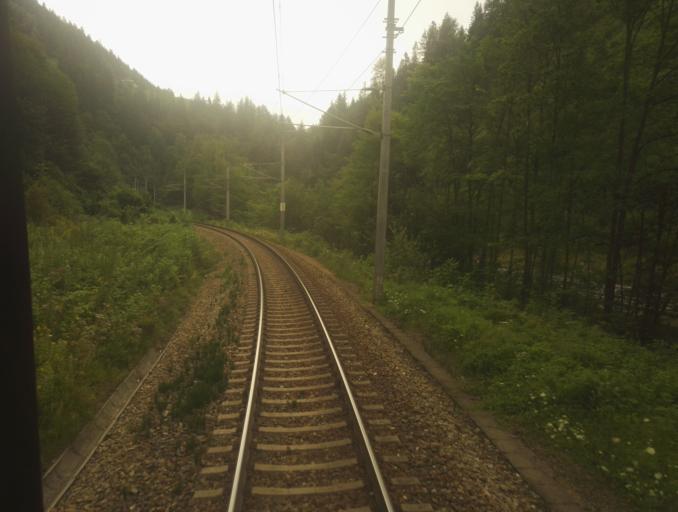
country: AT
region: Salzburg
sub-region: Politischer Bezirk Sankt Johann im Pongau
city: Huttau
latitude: 47.4300
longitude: 13.2688
